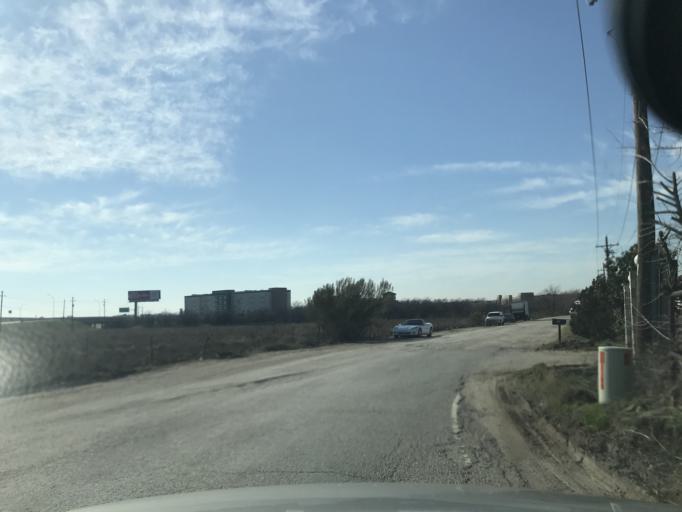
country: US
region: Texas
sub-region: Denton County
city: The Colony
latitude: 33.0835
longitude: -96.8534
